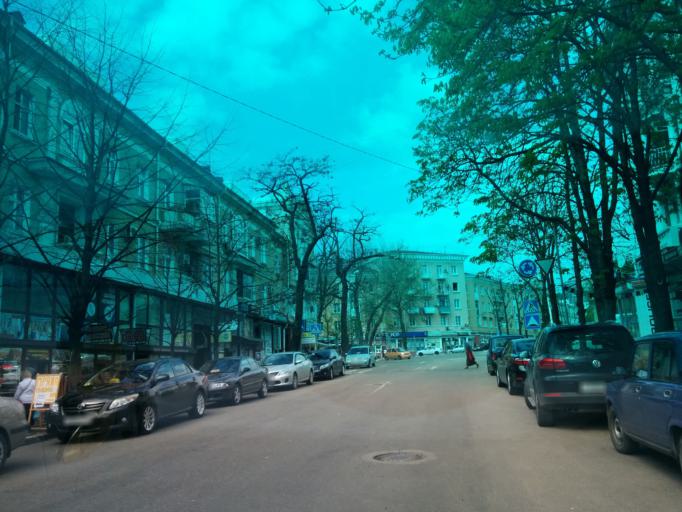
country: RU
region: Krasnodarskiy
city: Tuapse
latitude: 44.0988
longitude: 39.0801
